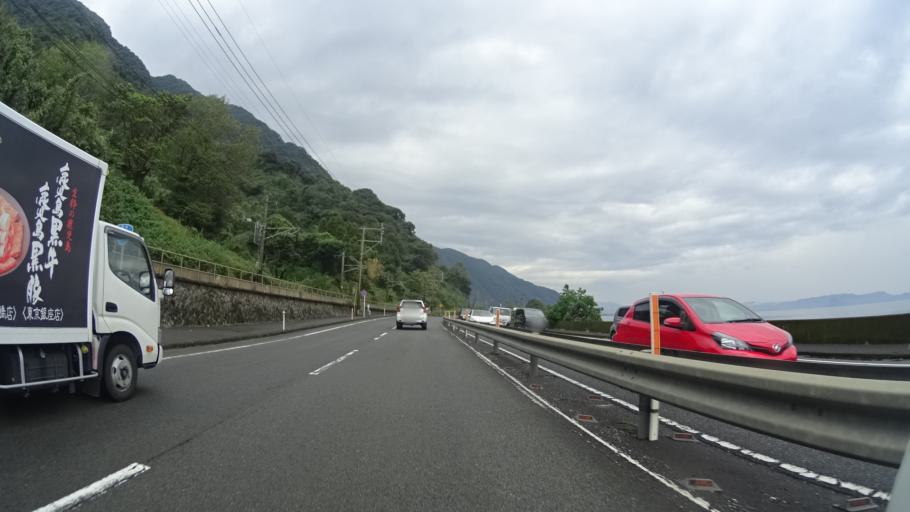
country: JP
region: Kagoshima
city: Kajiki
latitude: 31.6679
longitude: 130.6126
